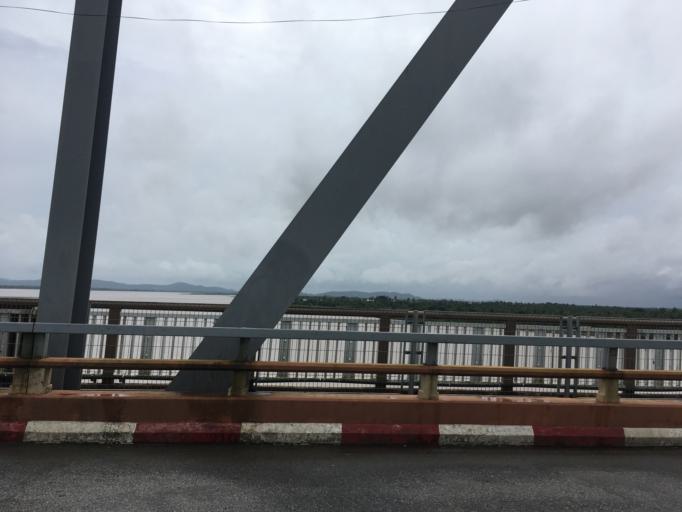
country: MM
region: Mon
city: Martaban
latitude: 16.5160
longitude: 97.6157
